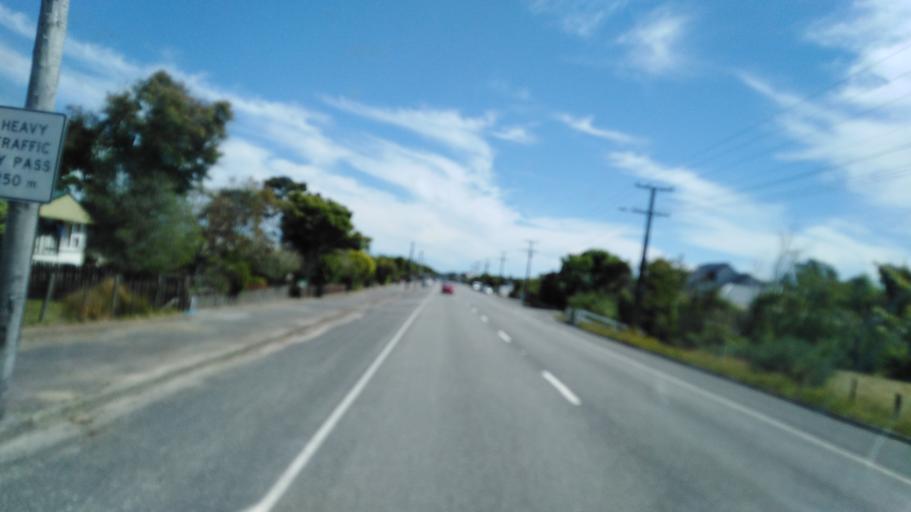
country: NZ
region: West Coast
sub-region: Buller District
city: Westport
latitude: -41.7535
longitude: 171.6140
